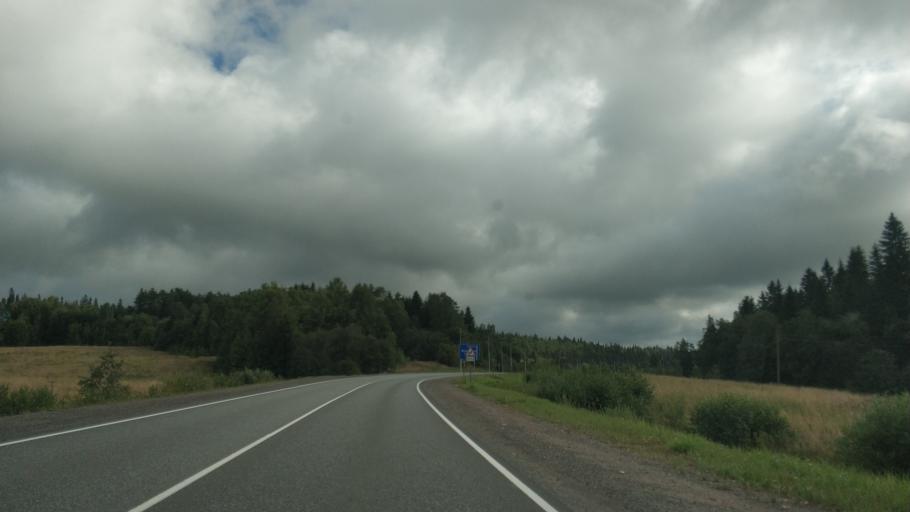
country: RU
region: Republic of Karelia
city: Khelyulya
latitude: 61.7732
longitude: 30.6560
